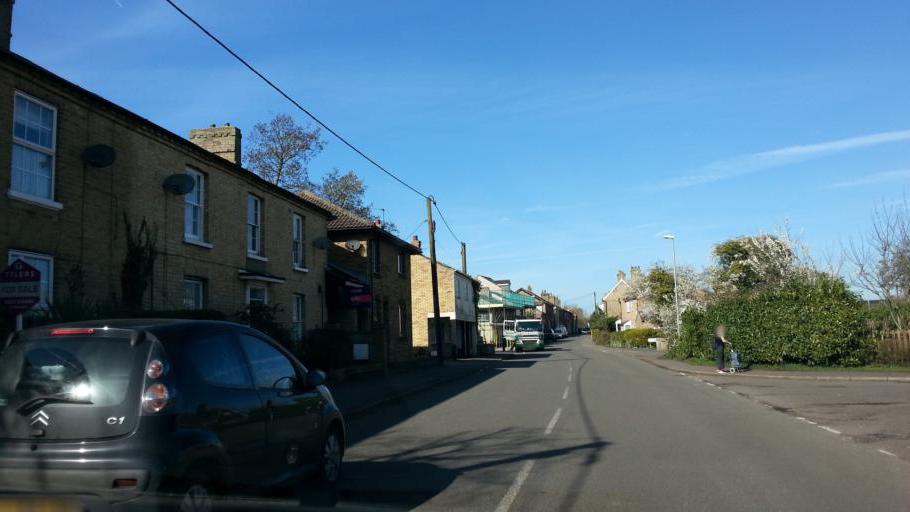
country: GB
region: England
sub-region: Cambridgeshire
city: Swavesey
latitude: 52.2992
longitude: -0.0034
